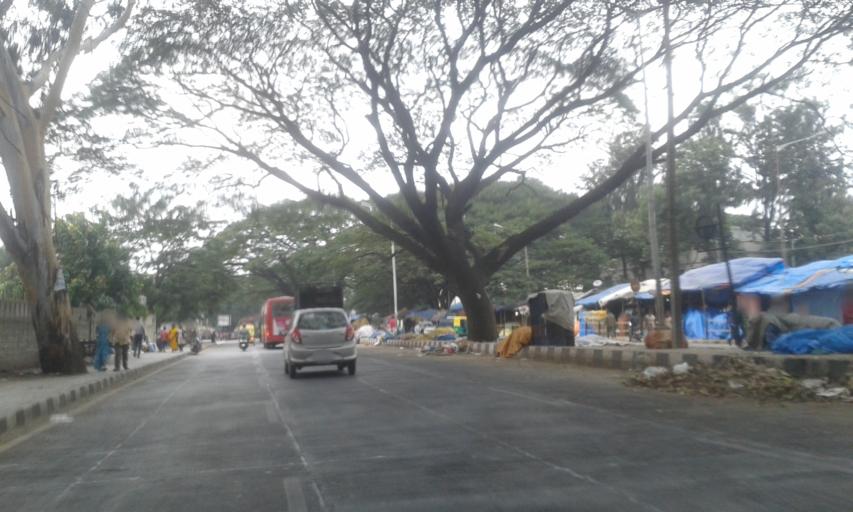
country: IN
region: Karnataka
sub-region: Bangalore Urban
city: Bangalore
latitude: 12.9225
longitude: 77.6229
